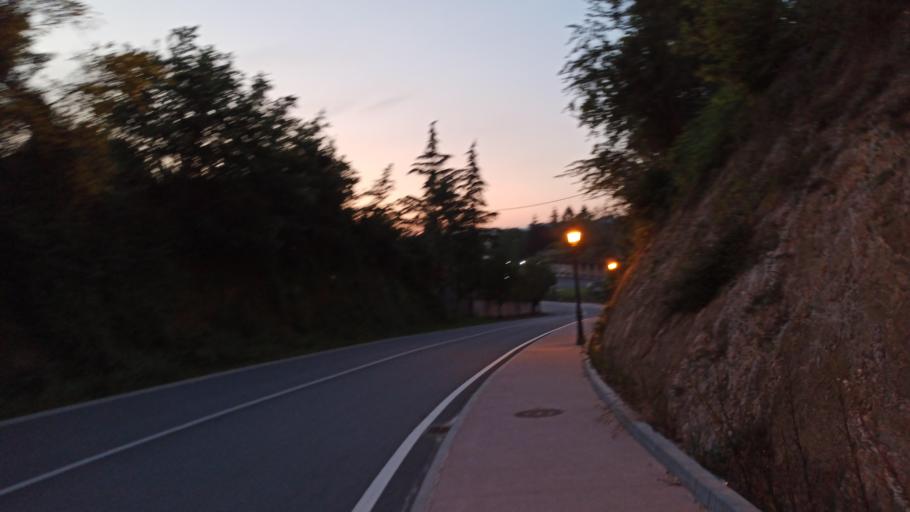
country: ES
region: Galicia
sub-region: Provincia da Coruna
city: Negreira
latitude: 42.9048
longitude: -8.7381
